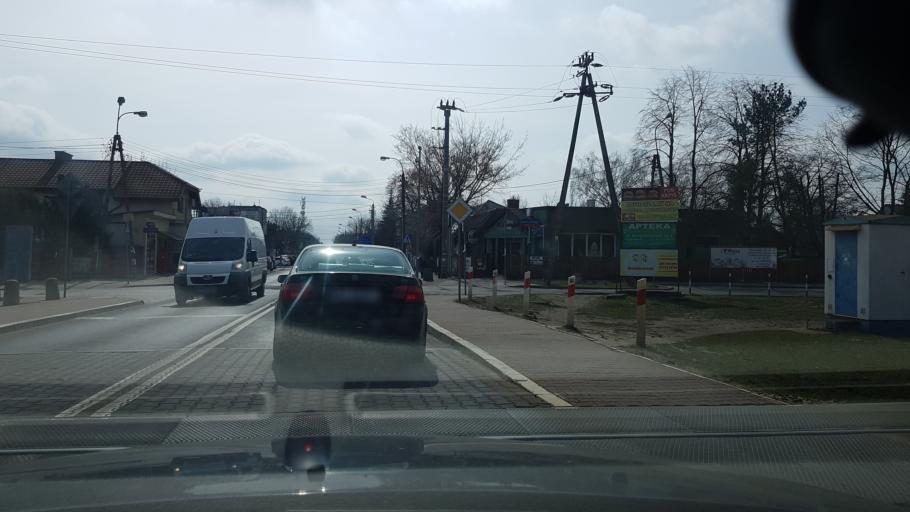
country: PL
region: Masovian Voivodeship
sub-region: Warszawa
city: Wesola
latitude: 52.2541
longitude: 21.2242
